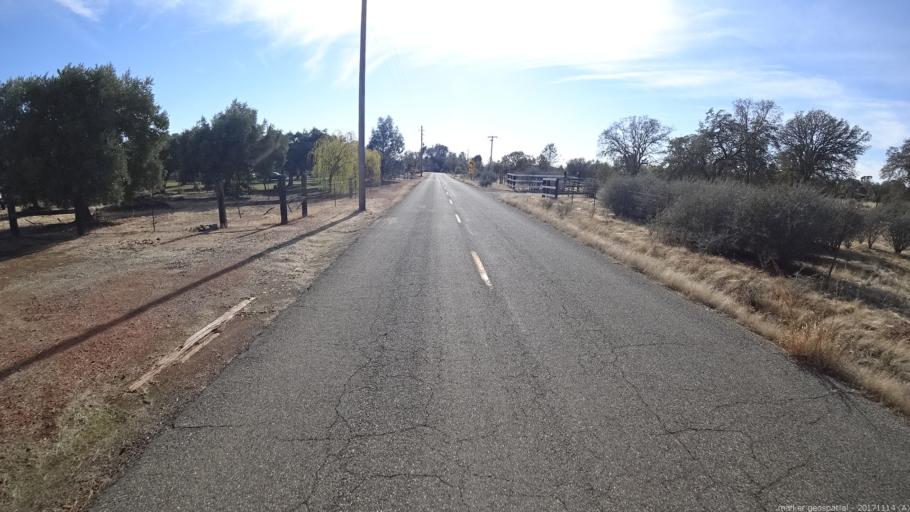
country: US
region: California
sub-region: Shasta County
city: Anderson
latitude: 40.4341
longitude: -122.4264
